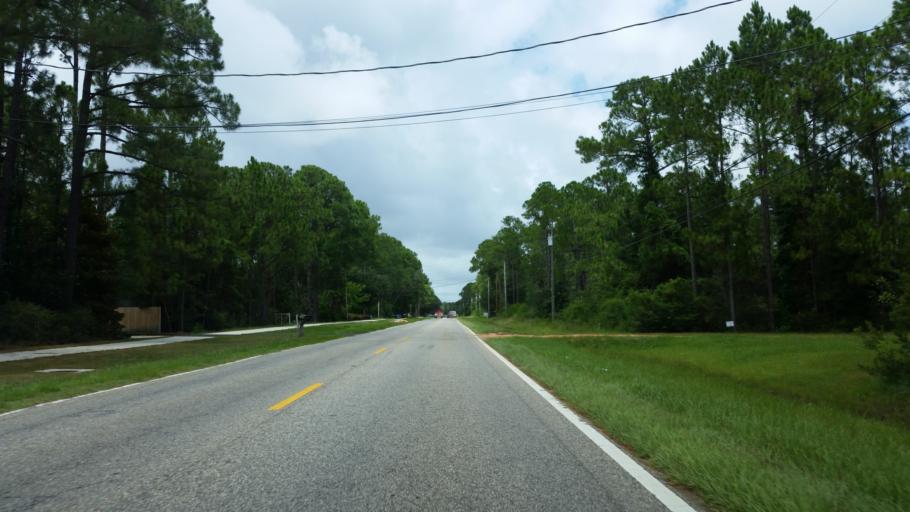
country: US
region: Florida
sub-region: Santa Rosa County
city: Woodlawn Beach
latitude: 30.4156
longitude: -86.9845
